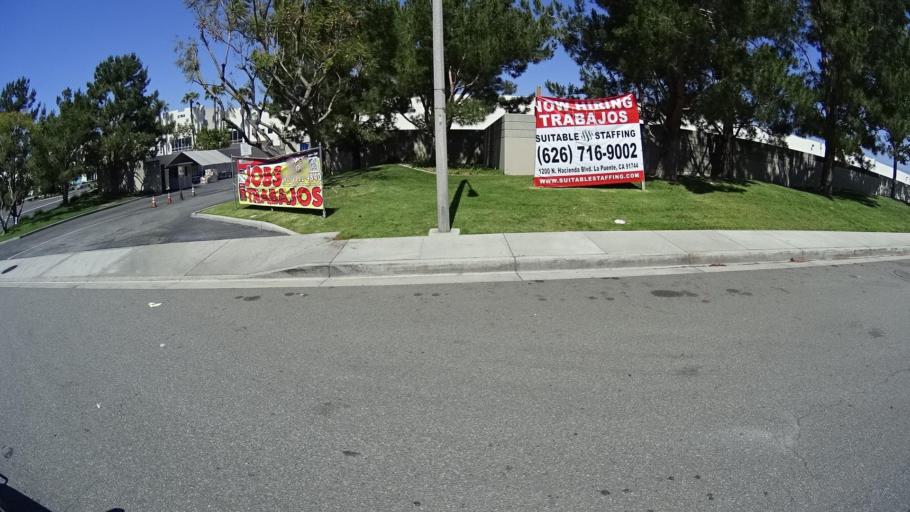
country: US
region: California
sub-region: Los Angeles County
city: Diamond Bar
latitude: 34.0179
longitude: -117.8311
